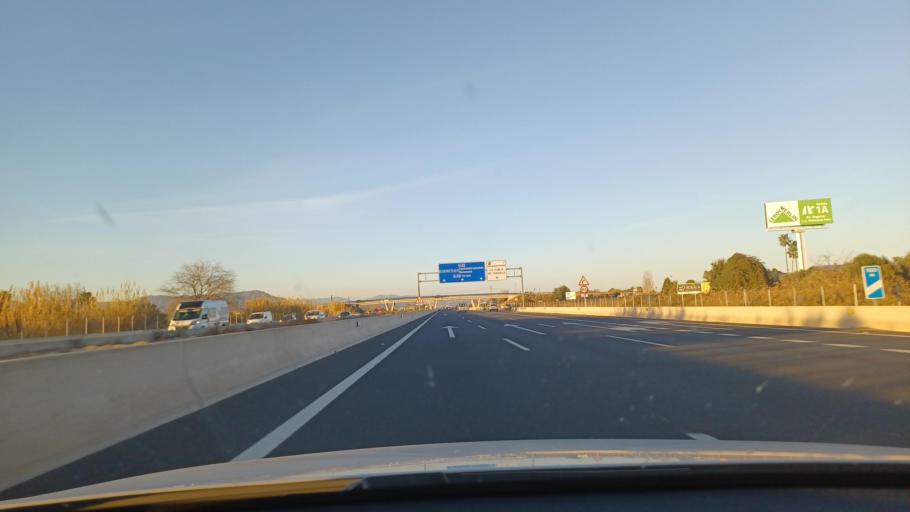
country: ES
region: Valencia
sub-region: Provincia de Valencia
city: Puig
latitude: 39.5655
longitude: -0.2961
